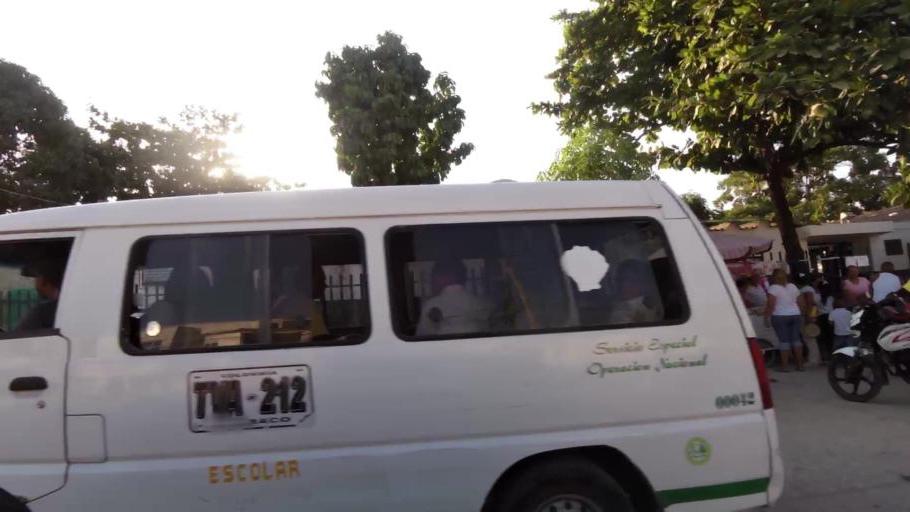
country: CO
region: Bolivar
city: Cartagena
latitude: 10.3855
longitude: -75.4780
